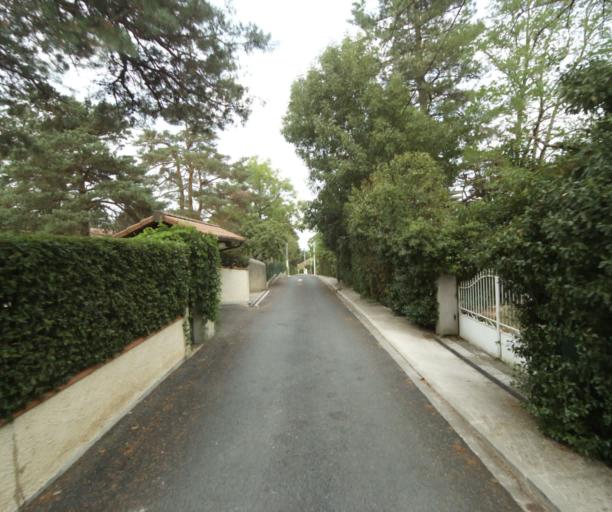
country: FR
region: Midi-Pyrenees
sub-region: Departement de la Haute-Garonne
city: Revel
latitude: 43.4400
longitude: 2.0212
